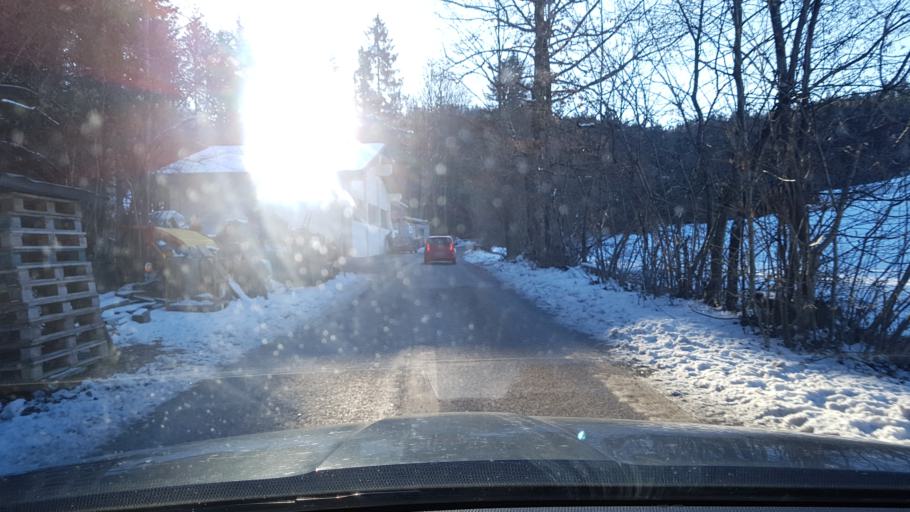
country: AT
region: Salzburg
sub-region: Politischer Bezirk Hallein
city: Scheffau am Tennengebirge
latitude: 47.6486
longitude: 13.2177
